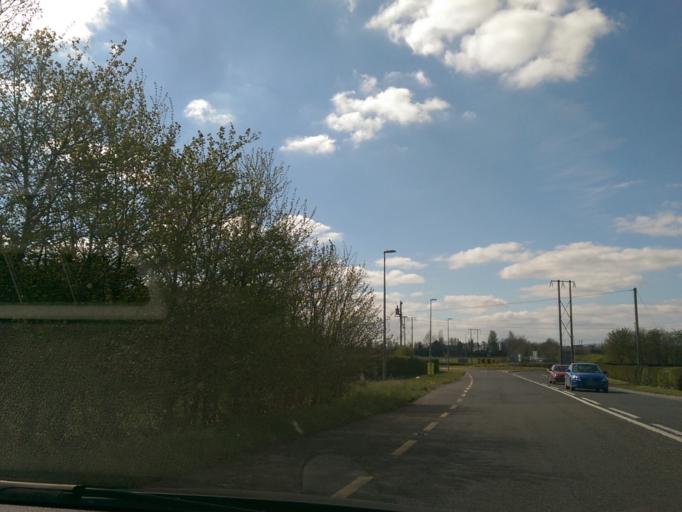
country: IE
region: Leinster
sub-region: Laois
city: Portlaoise
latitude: 53.0311
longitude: -7.2580
